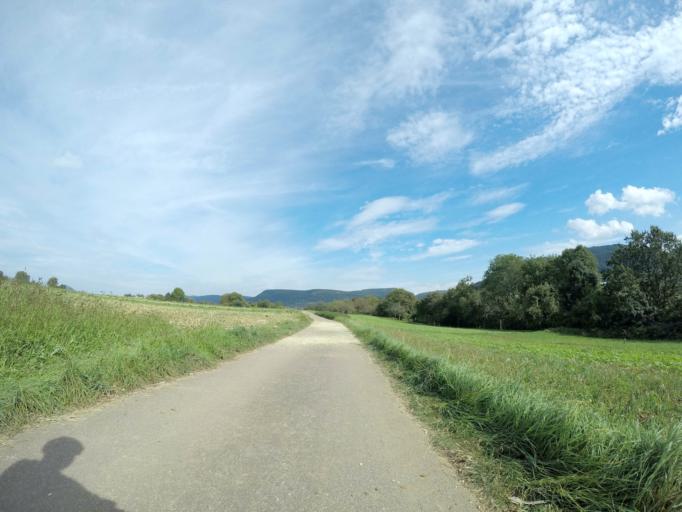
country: DE
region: Baden-Wuerttemberg
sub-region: Tuebingen Region
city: Pfullingen
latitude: 48.4550
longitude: 9.2024
